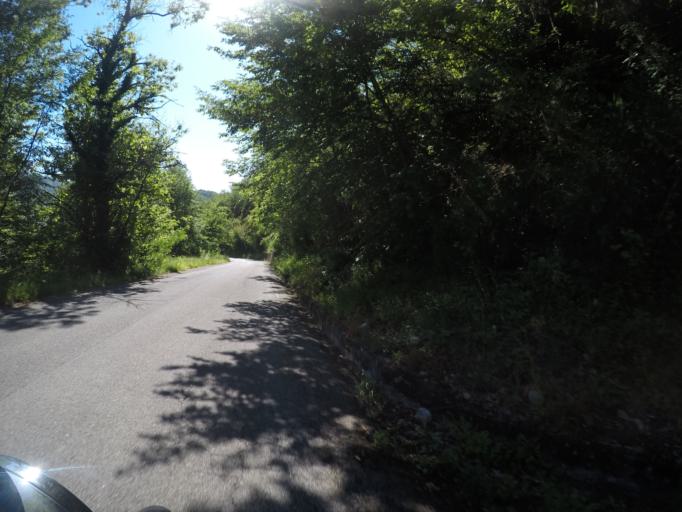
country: IT
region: Tuscany
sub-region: Provincia di Massa-Carrara
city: Fosdinovo
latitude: 44.1447
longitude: 10.0906
